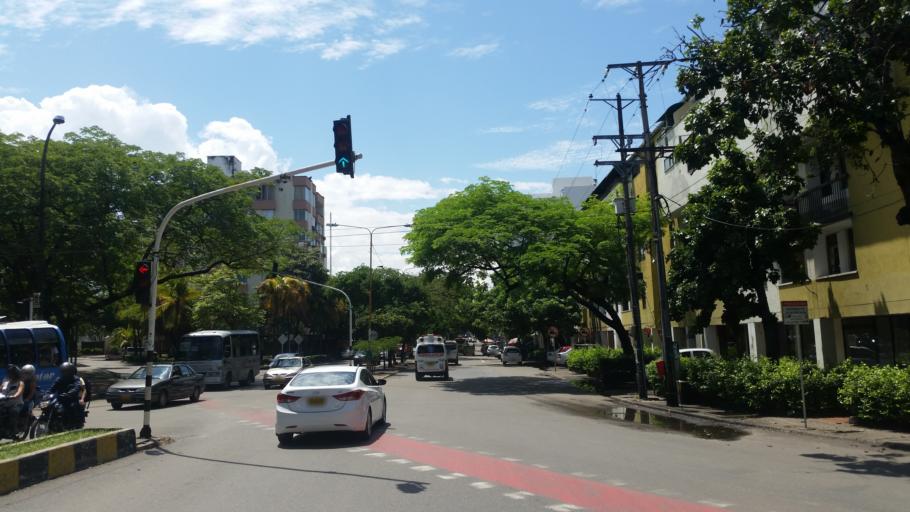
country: CO
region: Huila
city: Neiva
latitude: 2.9319
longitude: -75.2881
